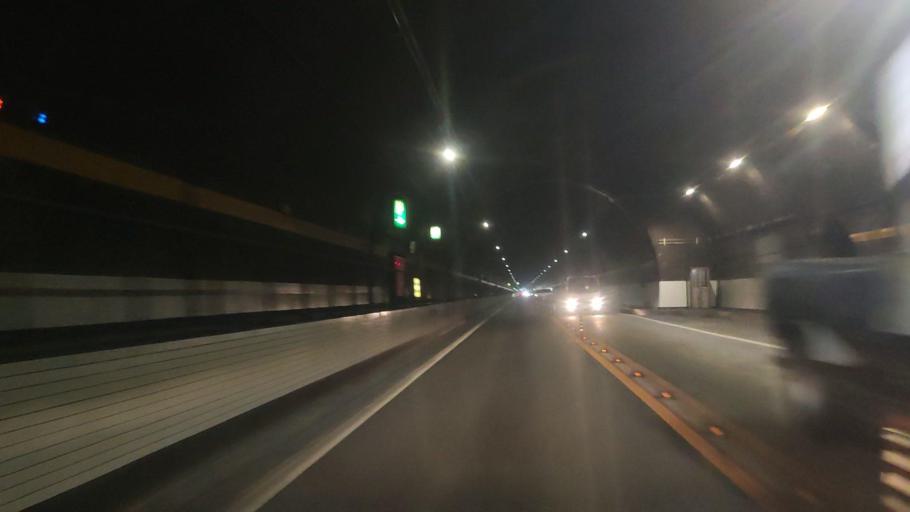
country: JP
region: Nagasaki
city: Nagasaki-shi
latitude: 32.7787
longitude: 129.8870
